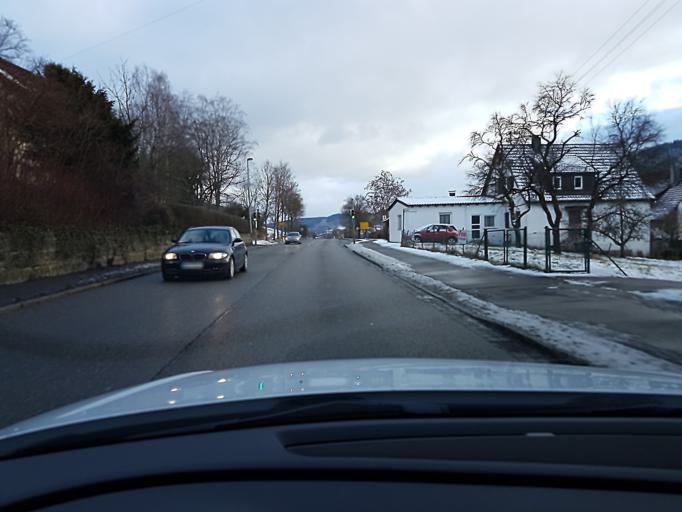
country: DE
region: Baden-Wuerttemberg
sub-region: Regierungsbezirk Stuttgart
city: Sulzbach an der Murr
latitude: 48.9960
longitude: 9.5356
